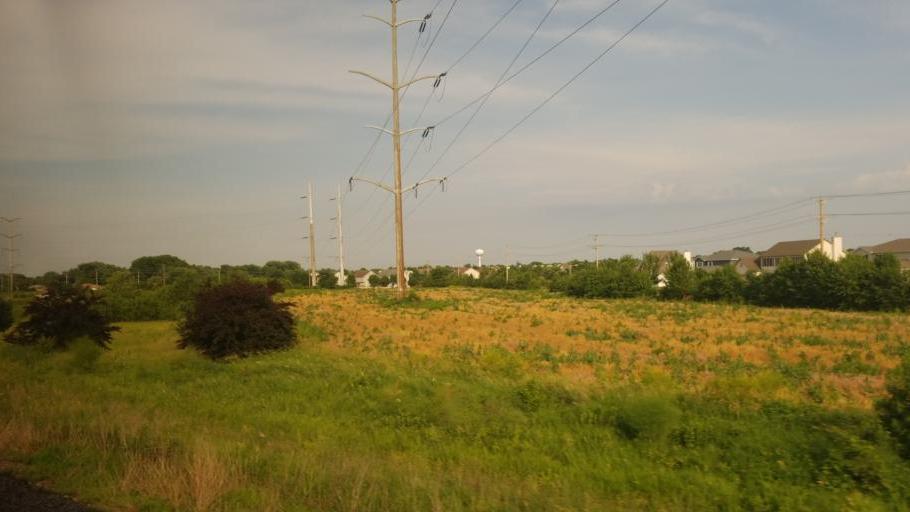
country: US
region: Illinois
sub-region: Kendall County
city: Lynwood
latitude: 41.7000
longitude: -88.3741
